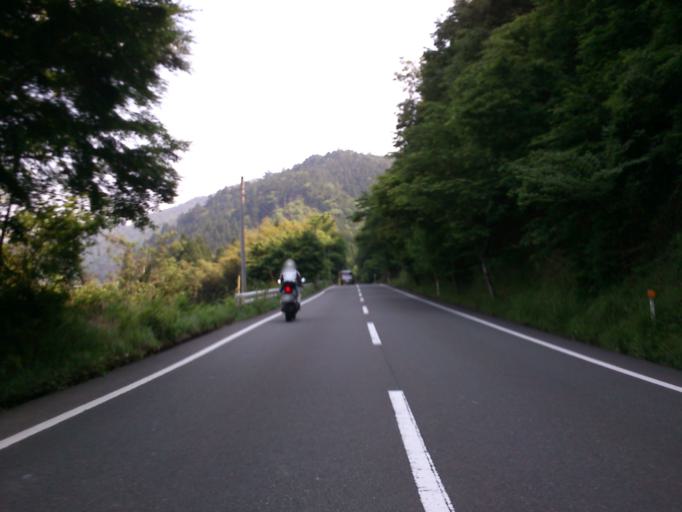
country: JP
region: Kyoto
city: Kameoka
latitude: 35.2440
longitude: 135.5586
